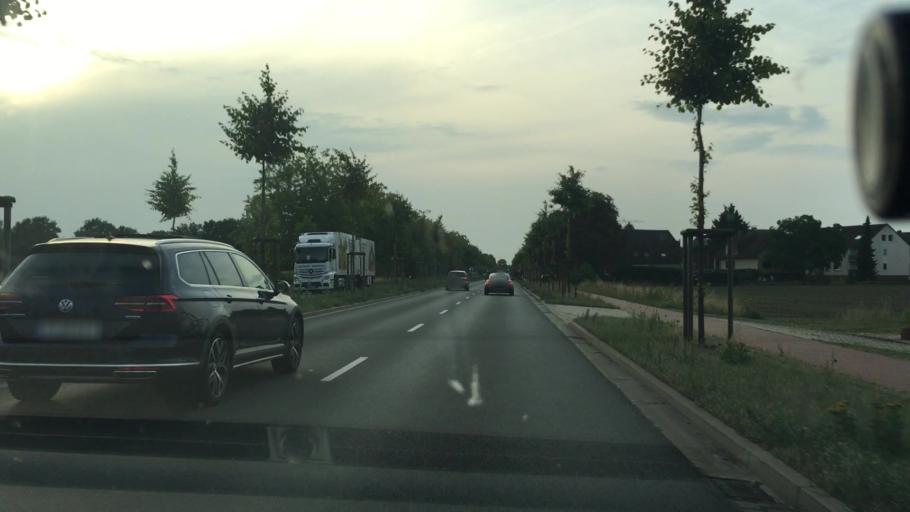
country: DE
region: Lower Saxony
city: Garbsen-Mitte
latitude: 52.4331
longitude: 9.6064
